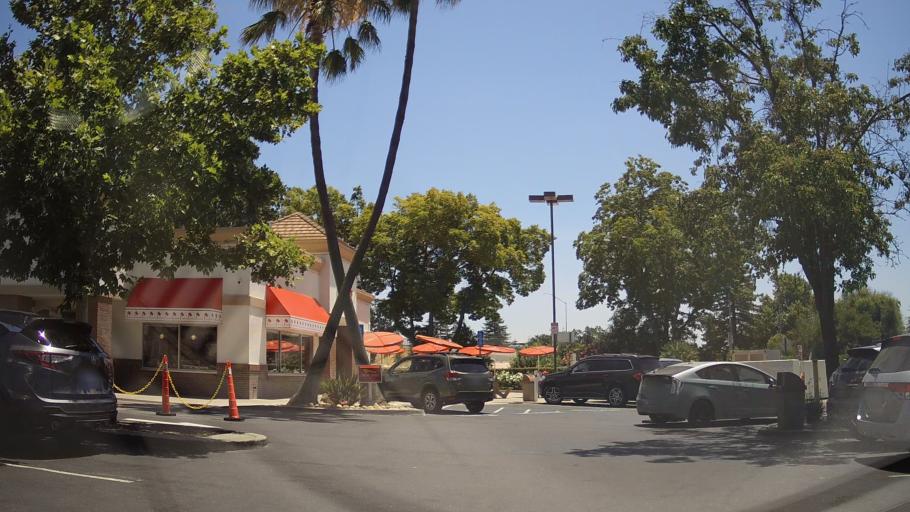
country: US
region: California
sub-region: Yolo County
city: Davis
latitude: 38.5411
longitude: -121.7376
